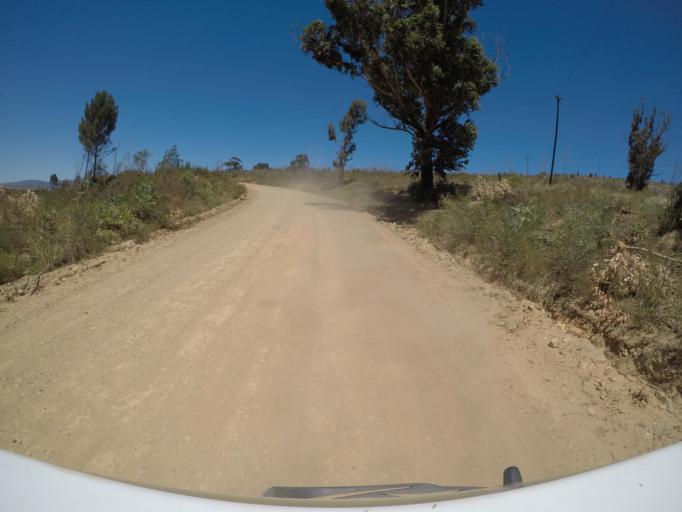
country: ZA
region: Western Cape
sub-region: Overberg District Municipality
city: Grabouw
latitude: -34.2185
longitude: 19.2039
